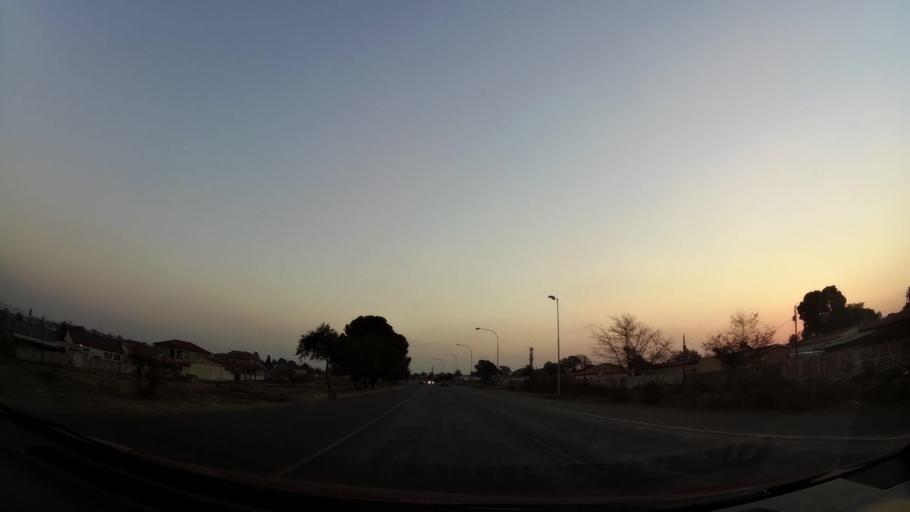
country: ZA
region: Gauteng
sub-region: City of Johannesburg Metropolitan Municipality
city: Soweto
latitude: -26.2926
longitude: 27.8790
